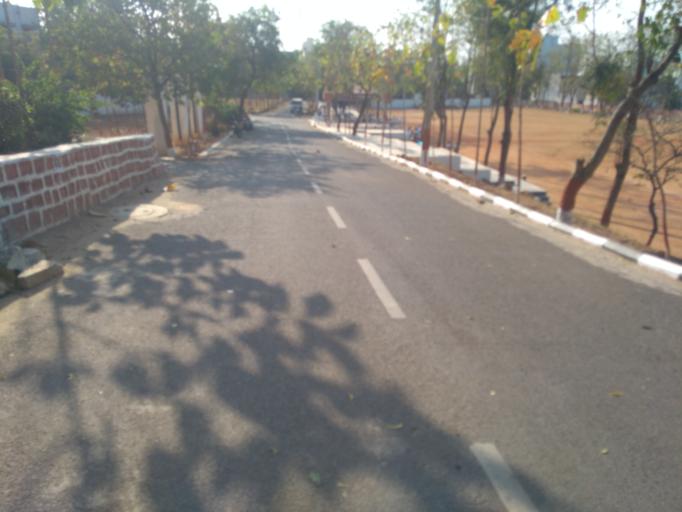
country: IN
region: Telangana
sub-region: Rangareddi
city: Gaddi Annaram
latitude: 17.3669
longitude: 78.4995
